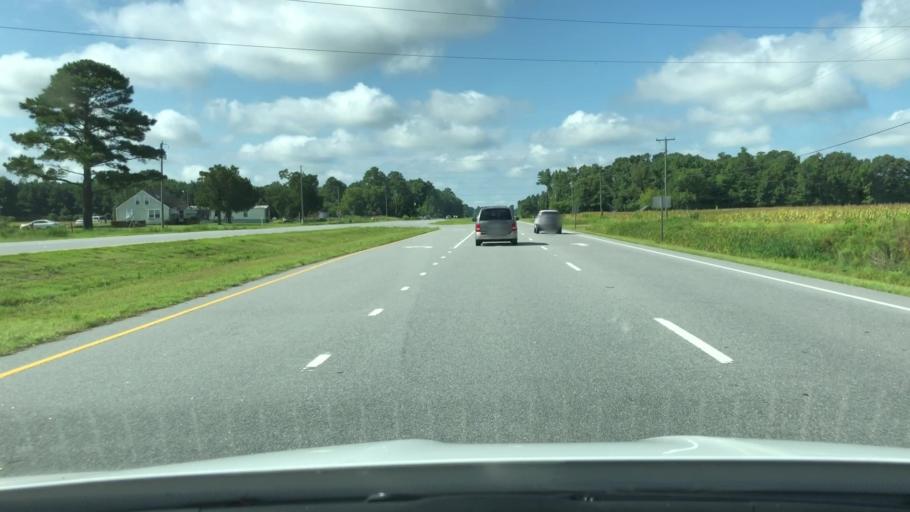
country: US
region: North Carolina
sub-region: Perquimans County
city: Hertford
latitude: 36.1483
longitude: -76.4875
